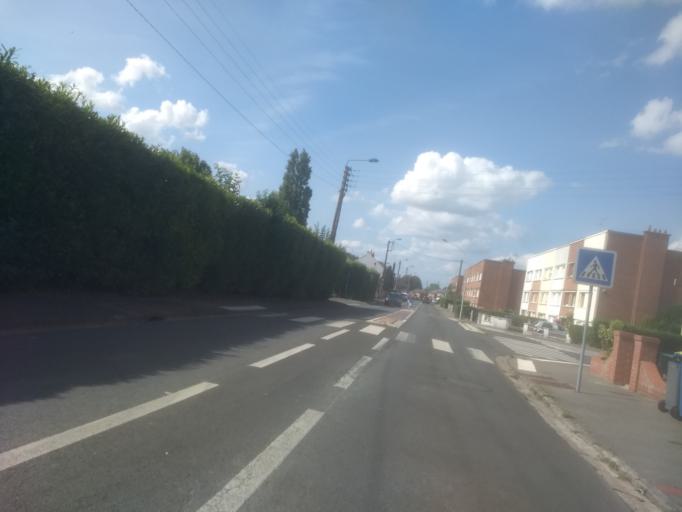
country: FR
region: Nord-Pas-de-Calais
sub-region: Departement du Pas-de-Calais
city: Beaurains
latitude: 50.2689
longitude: 2.7875
